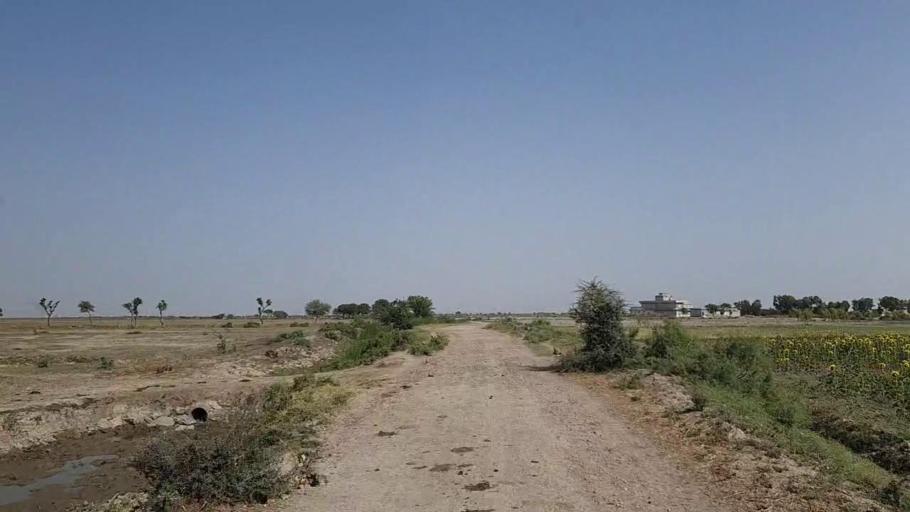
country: PK
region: Sindh
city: Jati
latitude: 24.3517
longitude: 68.3154
